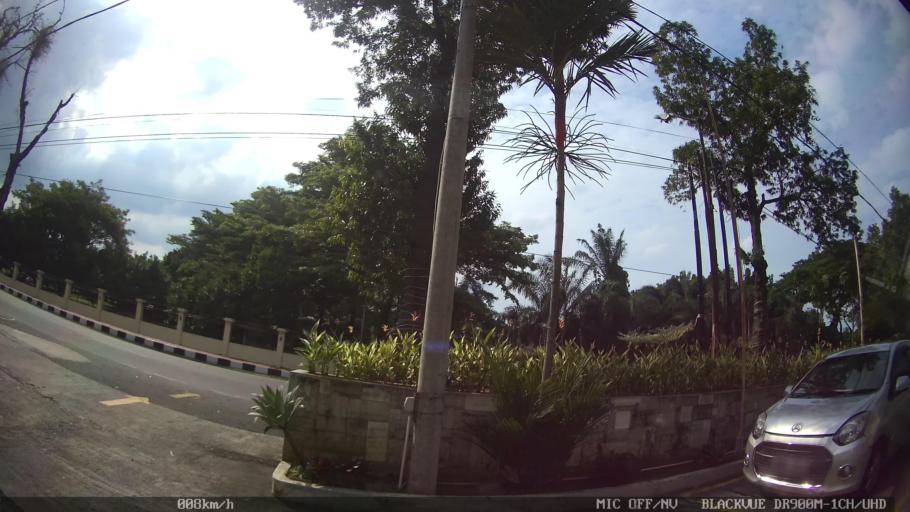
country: ID
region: North Sumatra
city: Medan
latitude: 3.5590
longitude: 98.6832
